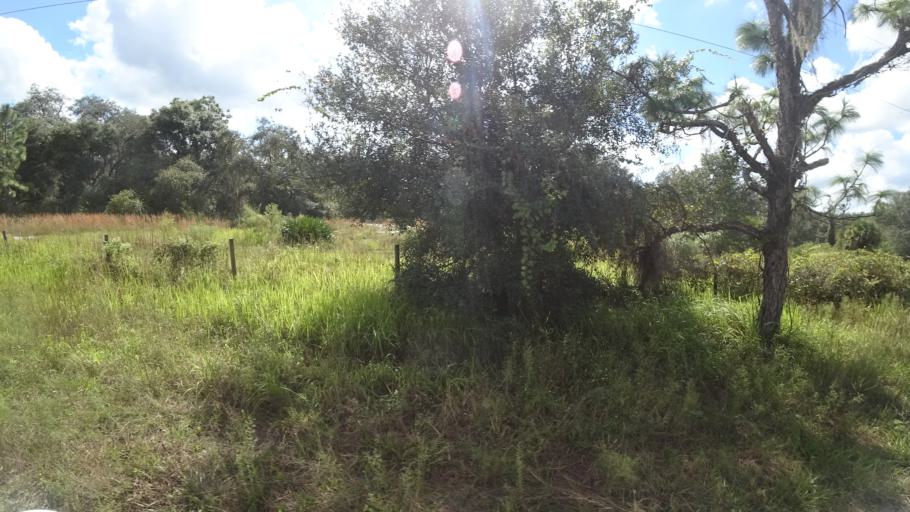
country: US
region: Florida
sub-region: Sarasota County
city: Lake Sarasota
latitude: 27.3204
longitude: -82.2558
